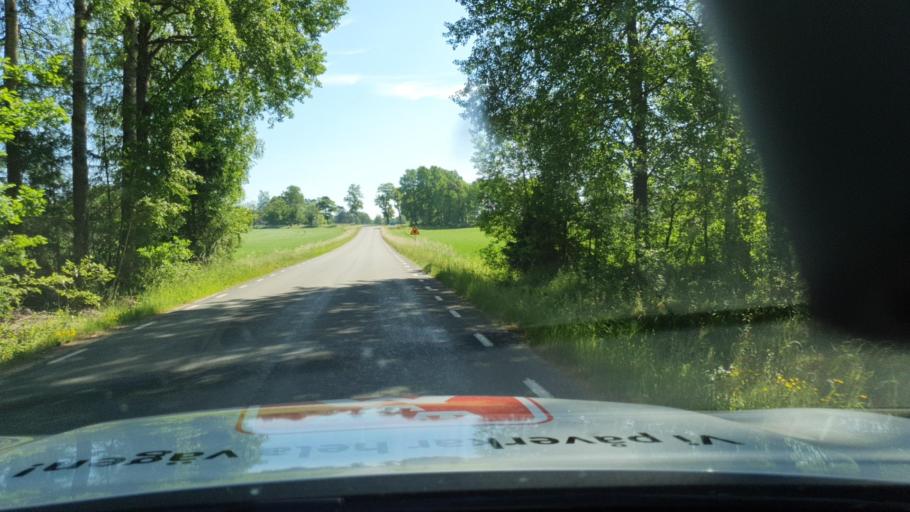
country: SE
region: Vaestra Goetaland
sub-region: Tidaholms Kommun
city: Tidaholm
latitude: 58.2594
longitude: 13.8904
